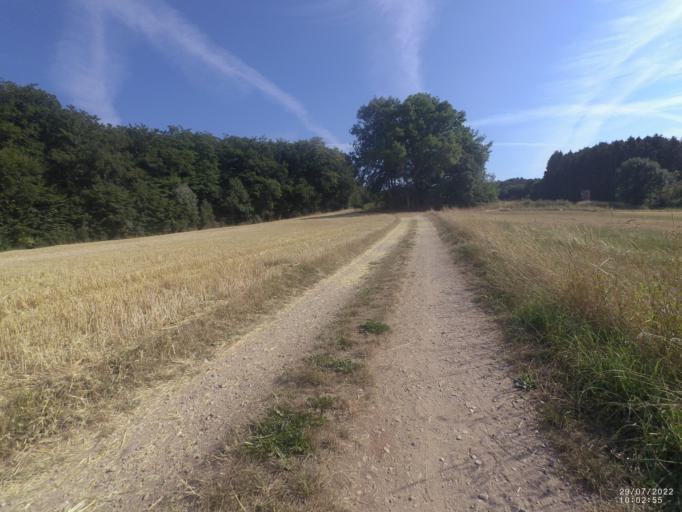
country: DE
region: Rheinland-Pfalz
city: Kalenborn-Scheuern
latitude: 50.2291
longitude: 6.5875
